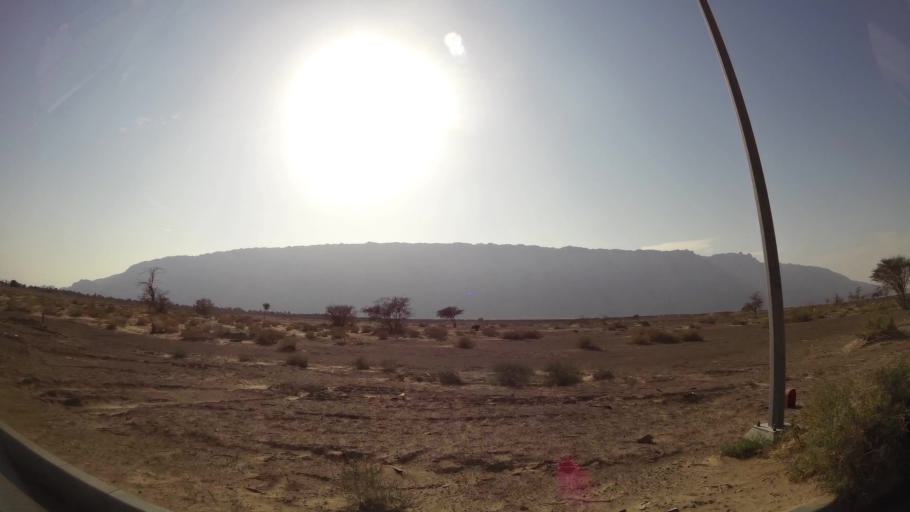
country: AE
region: Abu Dhabi
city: Al Ain
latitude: 24.0341
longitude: 55.8388
